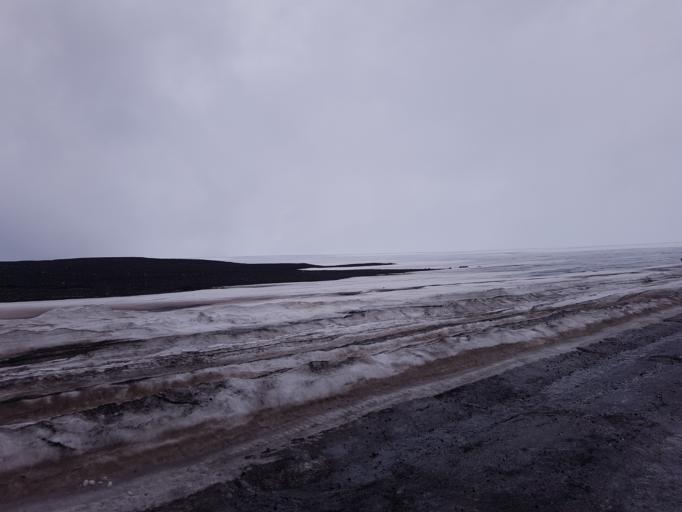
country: IS
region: South
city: Selfoss
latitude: 64.6422
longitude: -20.5562
